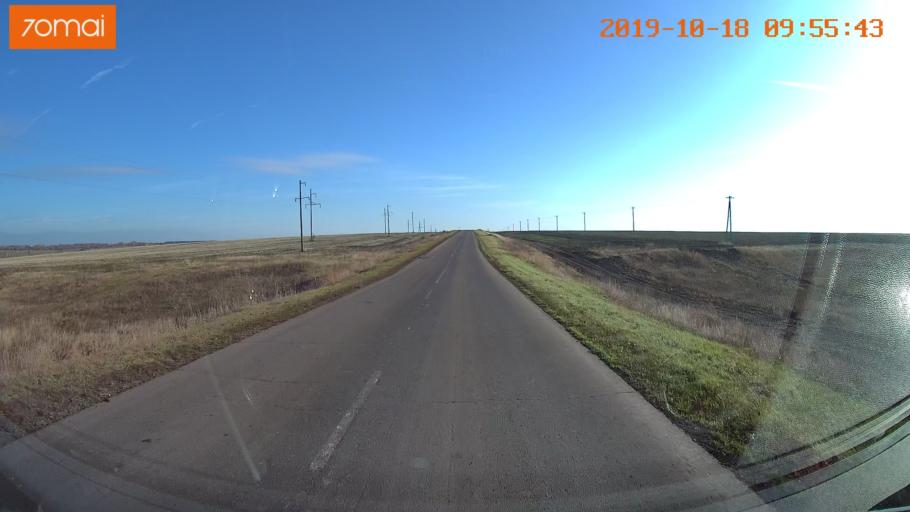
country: RU
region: Tula
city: Kurkino
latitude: 53.3716
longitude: 38.3713
